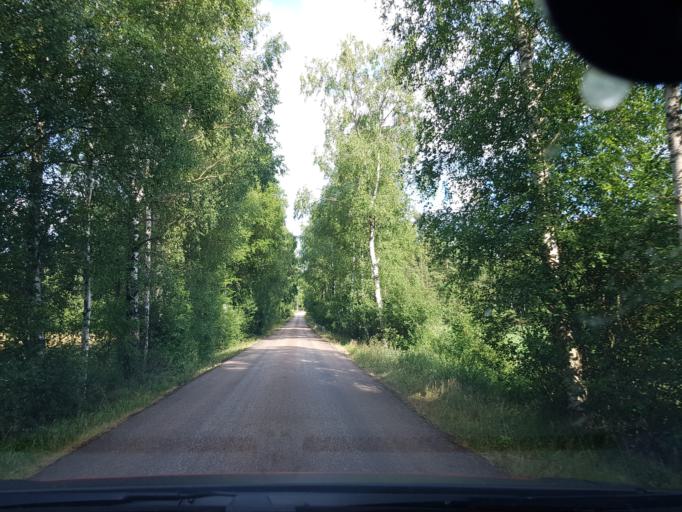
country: SE
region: Joenkoeping
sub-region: Gislaveds Kommun
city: Reftele
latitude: 57.2095
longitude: 13.5858
